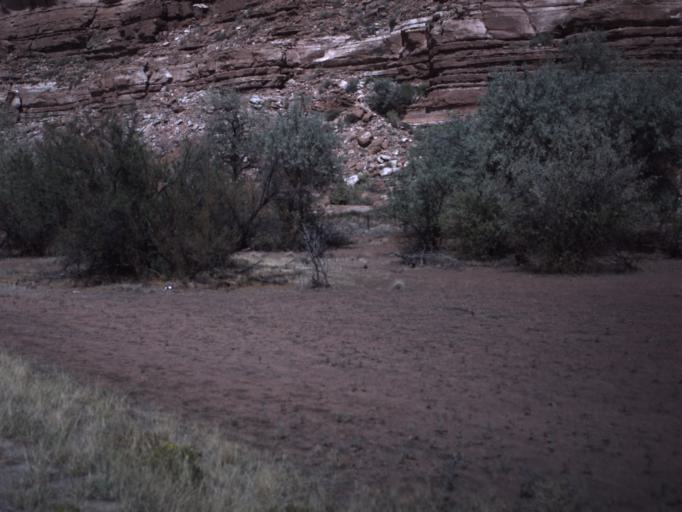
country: US
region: Utah
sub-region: San Juan County
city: Blanding
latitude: 37.2851
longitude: -109.5190
